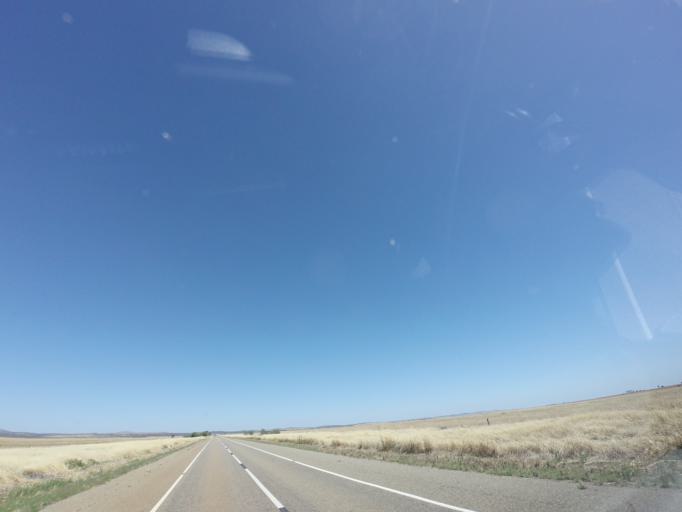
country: AU
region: South Australia
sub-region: Peterborough
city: Peterborough
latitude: -32.8248
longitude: 138.7019
